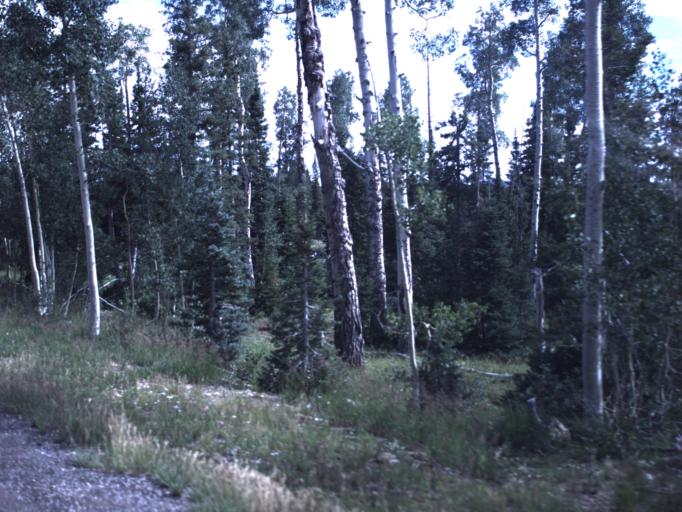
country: US
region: Utah
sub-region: Iron County
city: Parowan
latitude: 37.5550
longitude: -112.7896
